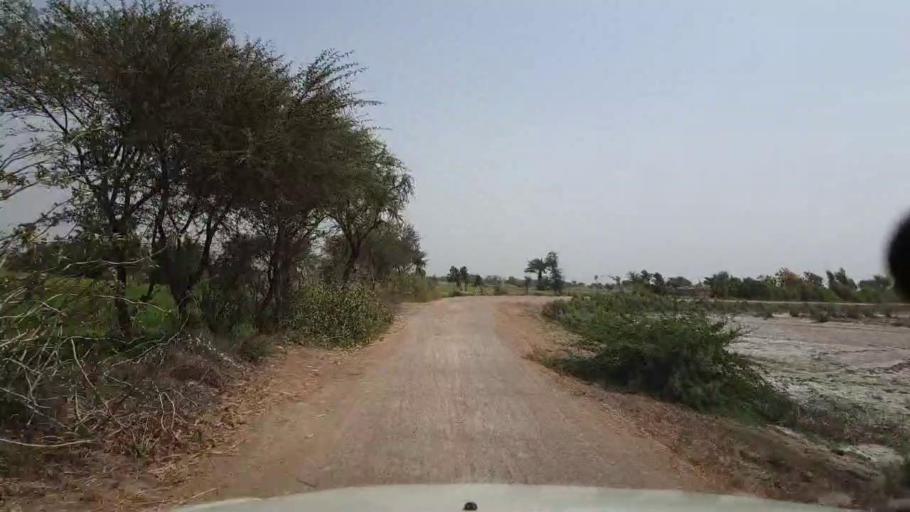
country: PK
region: Sindh
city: Matli
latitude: 25.0254
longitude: 68.7088
